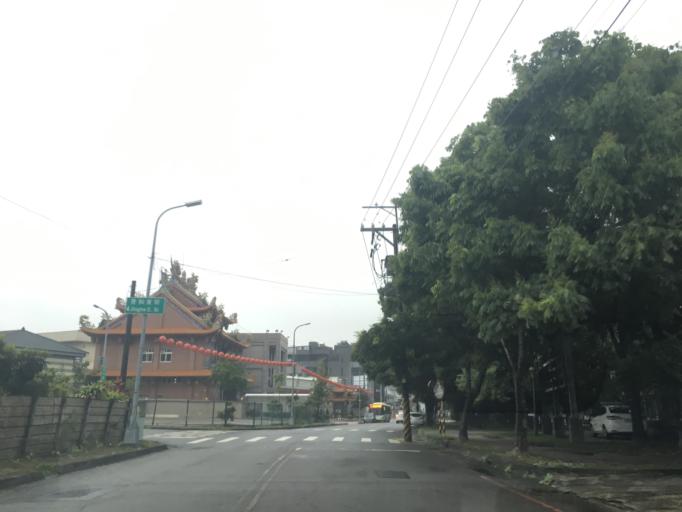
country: TW
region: Taiwan
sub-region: Taichung City
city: Taichung
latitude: 24.1685
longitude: 120.7129
